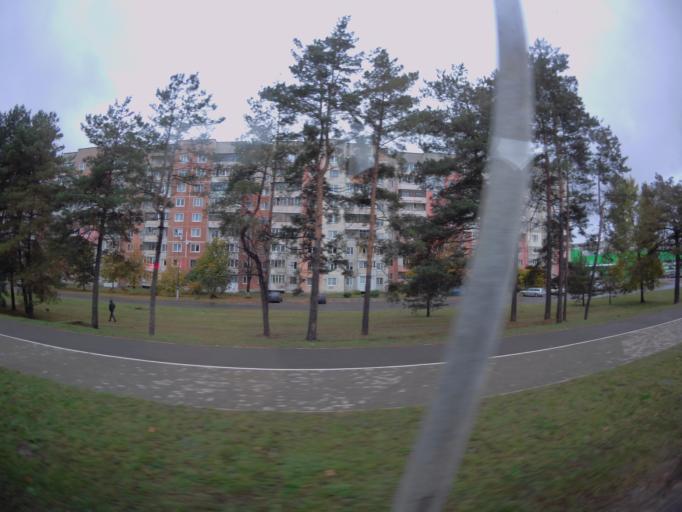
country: BY
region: Minsk
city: Horad Barysaw
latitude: 54.2019
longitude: 28.4800
